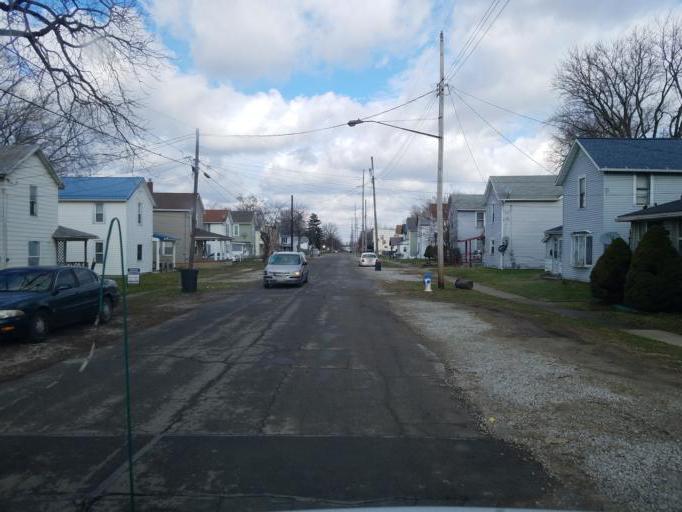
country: US
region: Ohio
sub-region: Marion County
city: Marion
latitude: 40.5792
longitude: -83.1418
